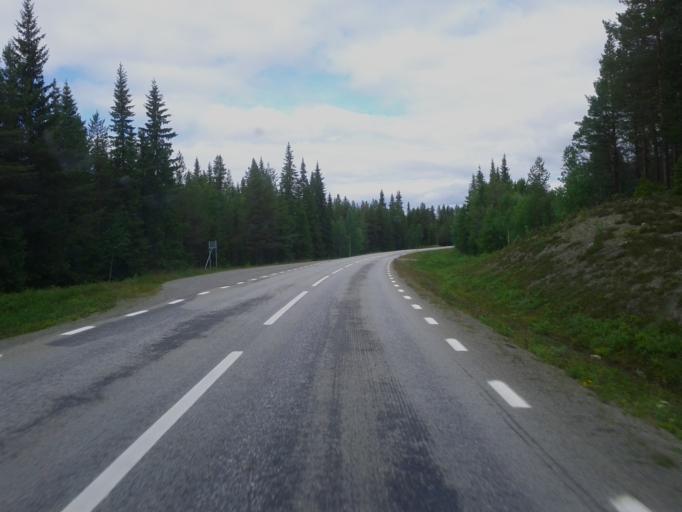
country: SE
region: Vaesterbotten
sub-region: Storumans Kommun
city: Fristad
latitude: 65.3673
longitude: 16.5212
